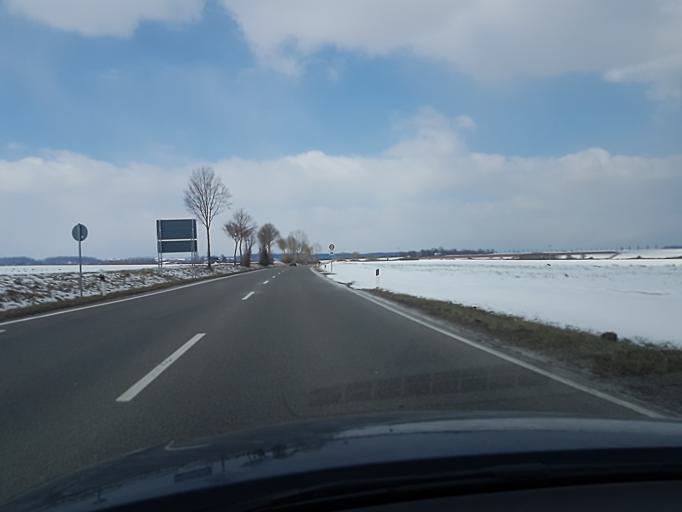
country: DE
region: Baden-Wuerttemberg
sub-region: Regierungsbezirk Stuttgart
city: Bondorf
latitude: 48.5365
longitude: 8.8431
